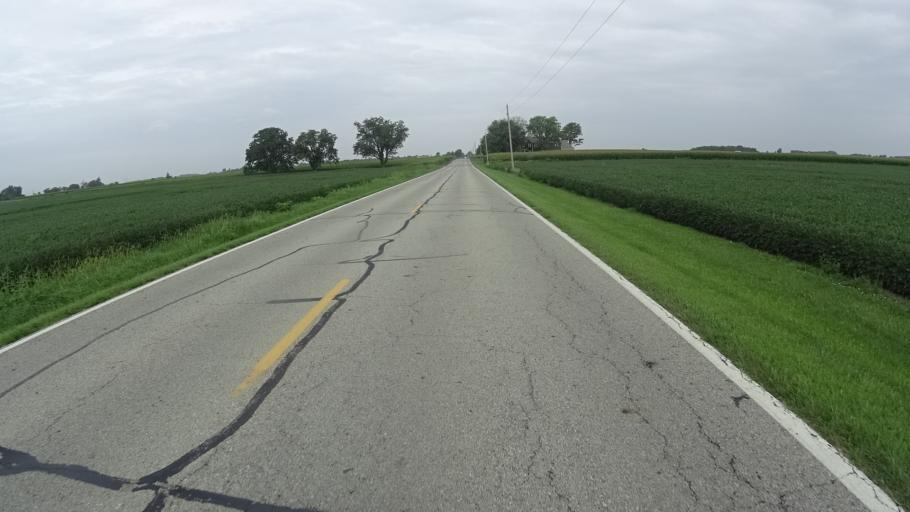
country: US
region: Indiana
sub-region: Madison County
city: Lapel
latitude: 40.0469
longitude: -85.8154
